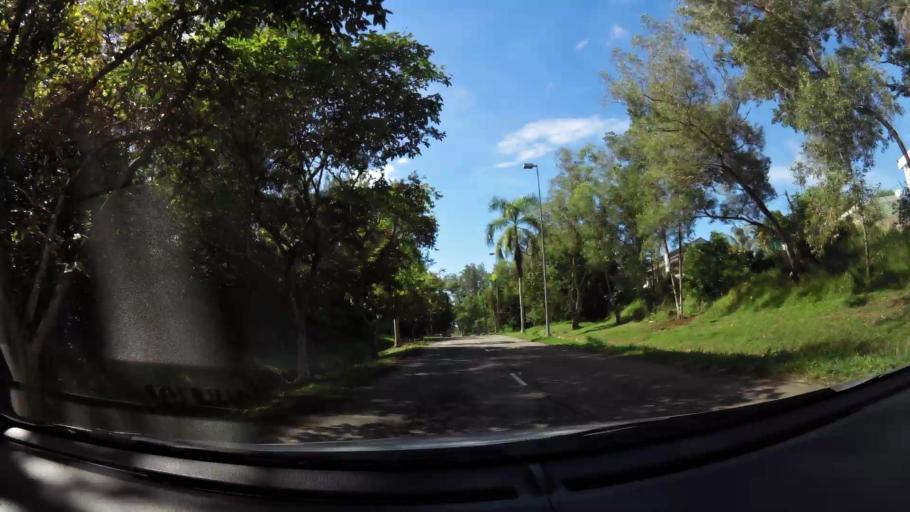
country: BN
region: Brunei and Muara
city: Bandar Seri Begawan
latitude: 4.9489
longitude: 114.9369
